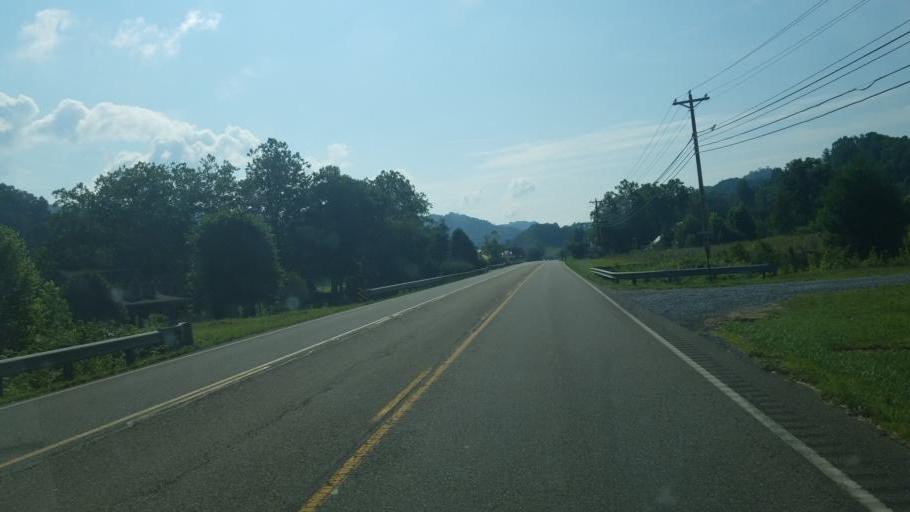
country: US
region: Tennessee
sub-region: Carter County
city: Roan Mountain
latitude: 36.1912
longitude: -82.0482
